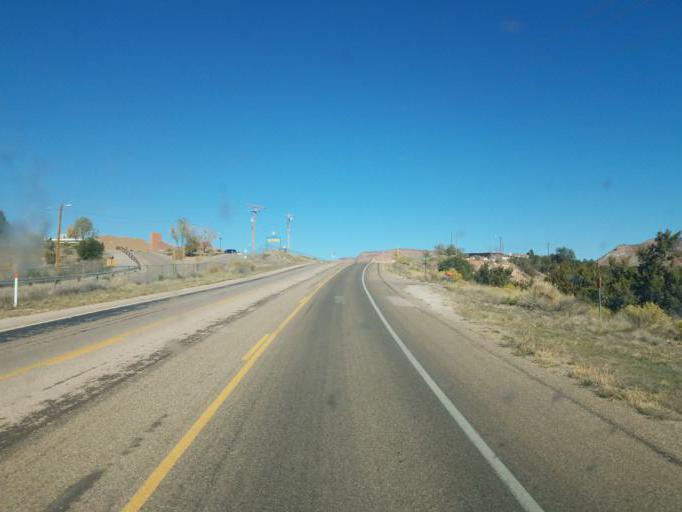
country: US
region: New Mexico
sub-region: Sandoval County
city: Jemez Pueblo
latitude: 35.6567
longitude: -106.7358
